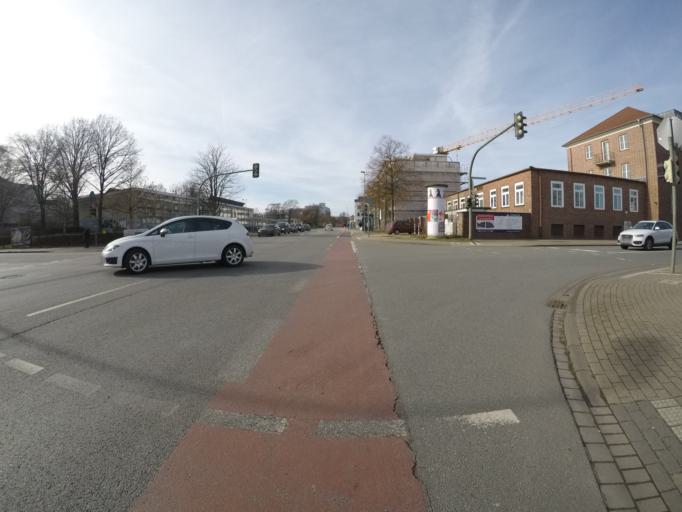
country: DE
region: North Rhine-Westphalia
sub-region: Regierungsbezirk Detmold
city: Bielefeld
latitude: 52.0254
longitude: 8.5484
